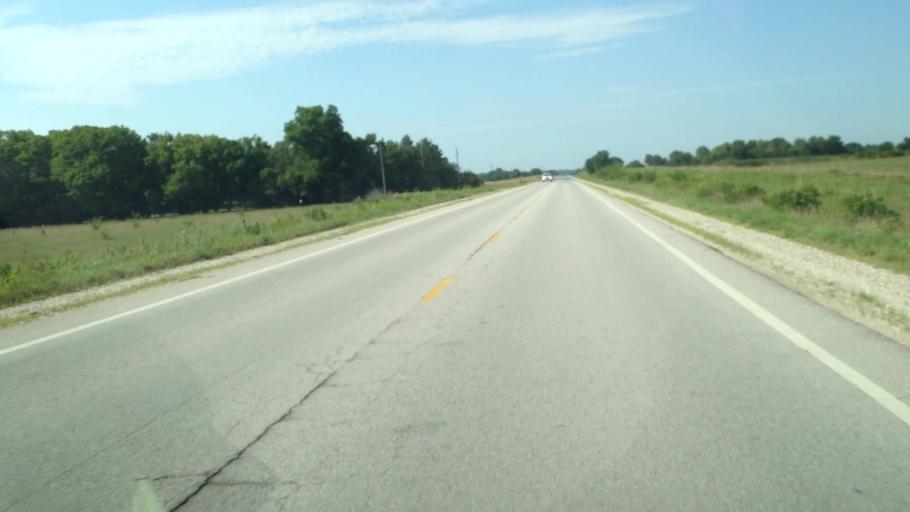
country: US
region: Kansas
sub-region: Neosho County
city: Erie
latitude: 37.4914
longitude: -95.2693
